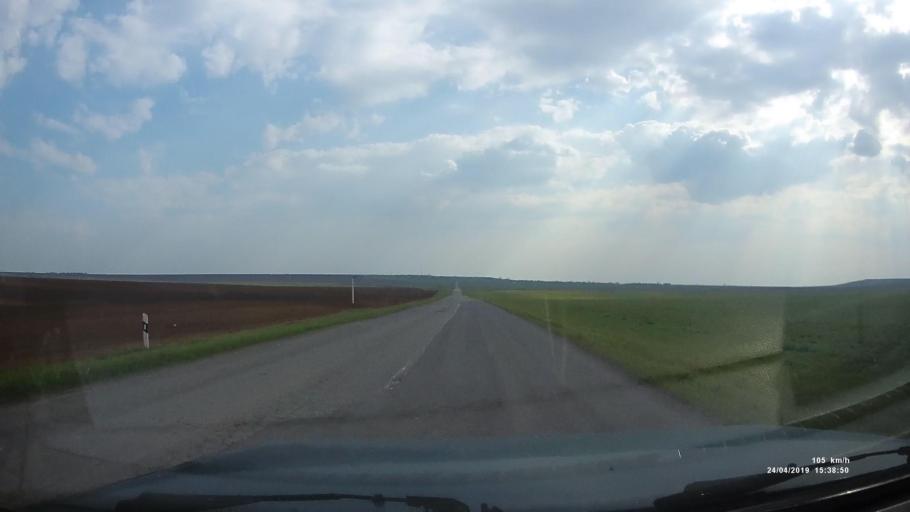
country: RU
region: Kalmykiya
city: Yashalta
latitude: 46.5930
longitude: 42.8225
